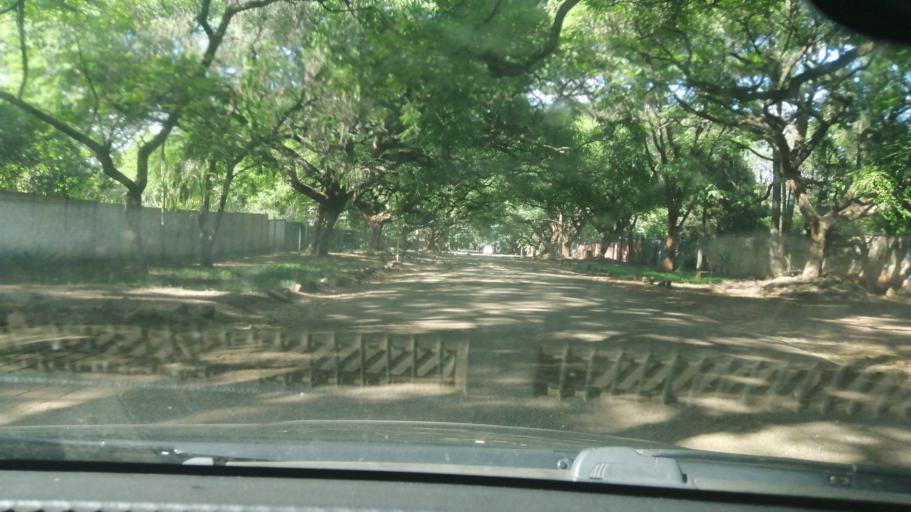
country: ZW
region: Harare
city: Harare
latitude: -17.7937
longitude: 31.0581
